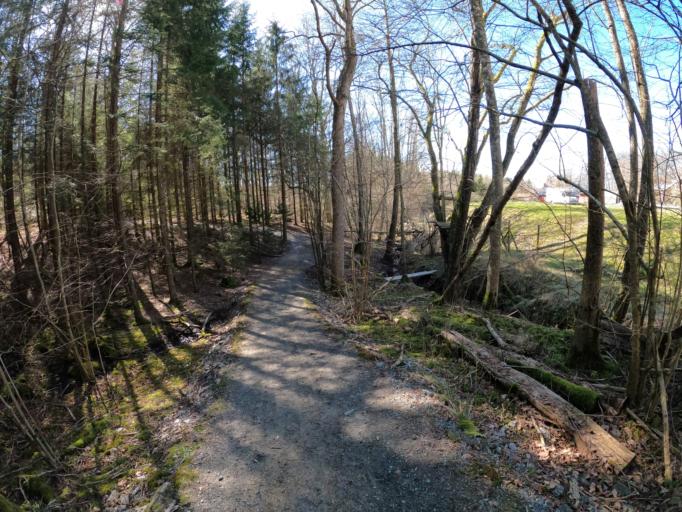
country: SE
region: Vaestra Goetaland
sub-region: Harryda Kommun
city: Molnlycke
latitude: 57.6264
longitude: 12.1117
